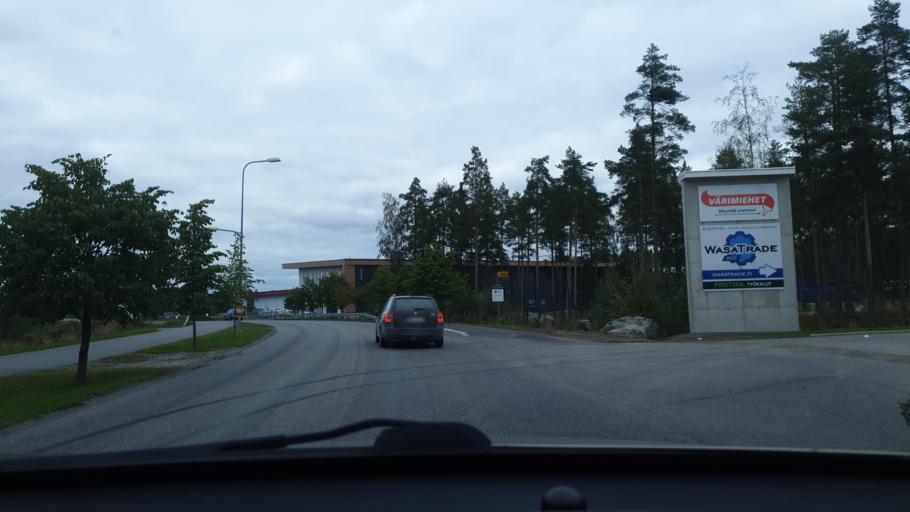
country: FI
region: Ostrobothnia
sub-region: Vaasa
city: Korsholm
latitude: 63.1151
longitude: 21.6602
